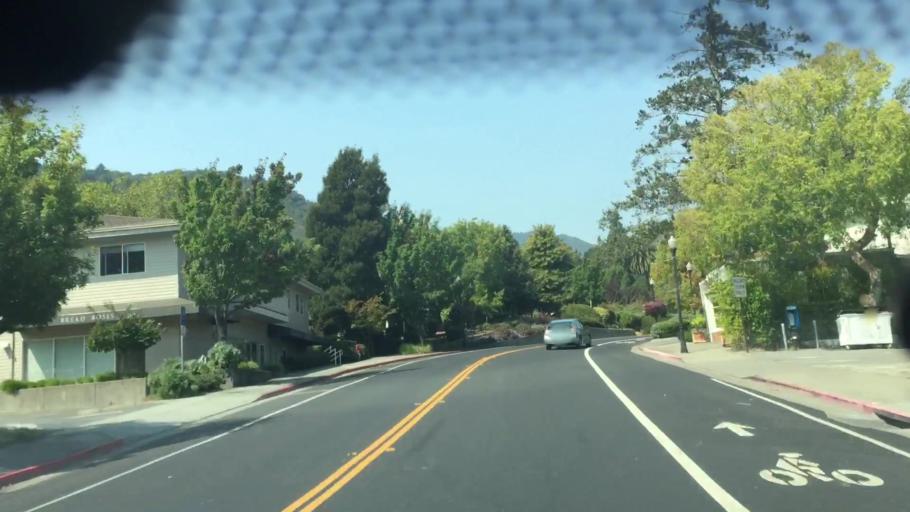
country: US
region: California
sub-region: Marin County
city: Corte Madera
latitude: 37.9256
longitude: -122.5280
